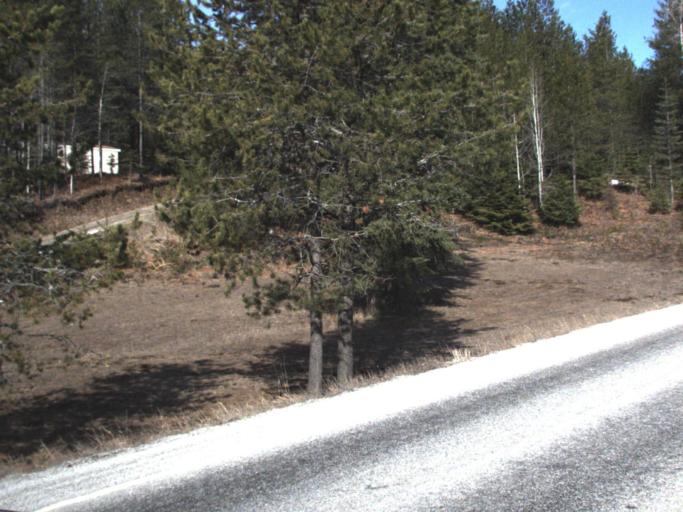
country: CA
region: British Columbia
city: Fruitvale
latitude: 48.6477
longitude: -117.3790
